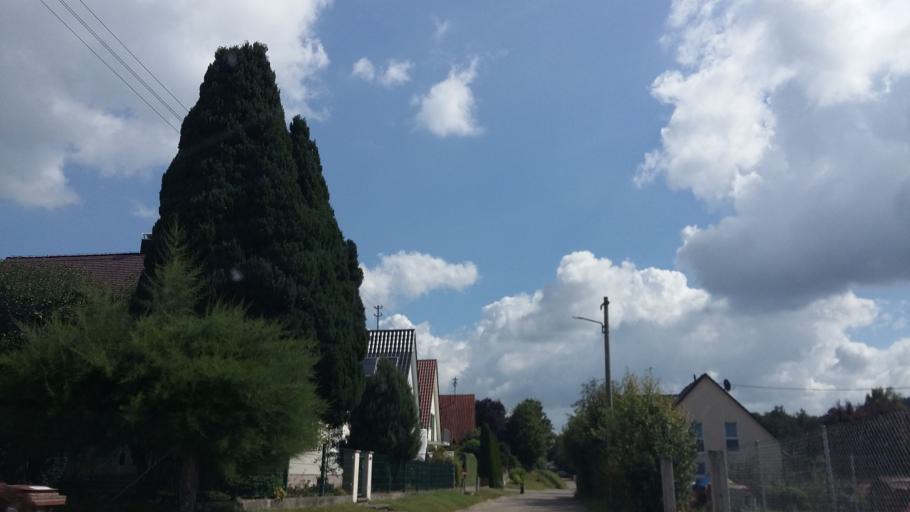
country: DE
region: Bavaria
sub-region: Swabia
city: Jettingen-Scheppach
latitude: 48.4034
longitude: 10.4519
